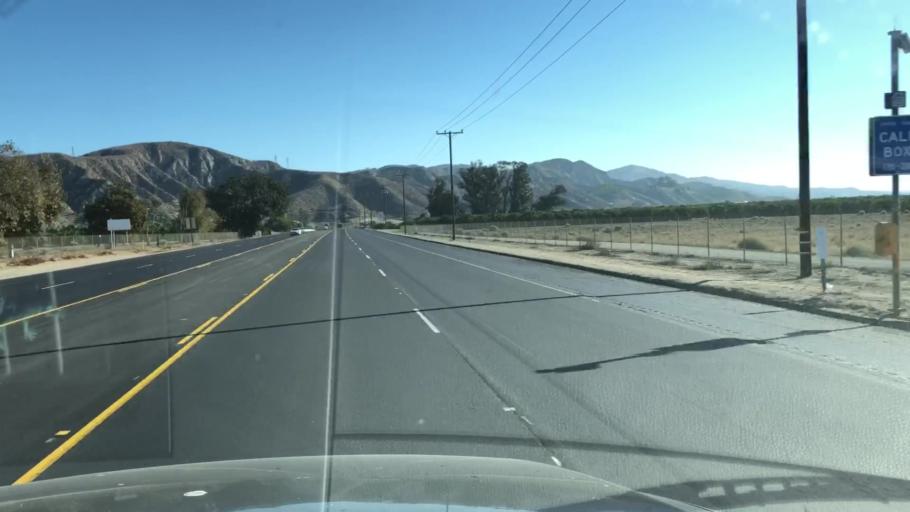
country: US
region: California
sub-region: Ventura County
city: Piru
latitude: 34.4069
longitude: -118.7912
